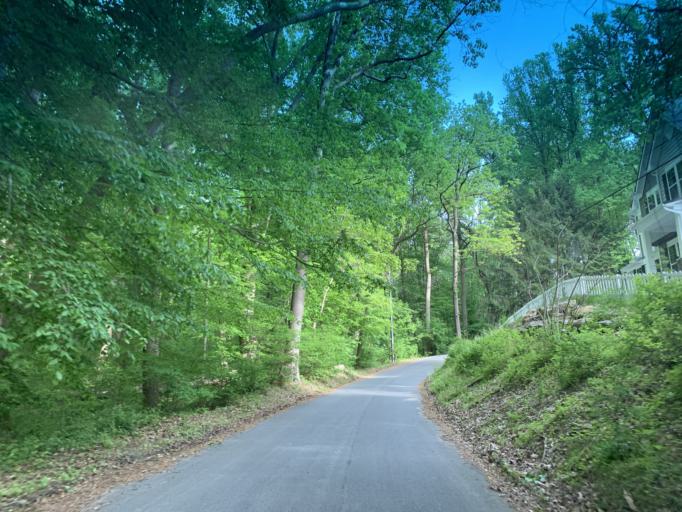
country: US
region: Maryland
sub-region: Baltimore County
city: Perry Hall
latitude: 39.4544
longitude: -76.4641
